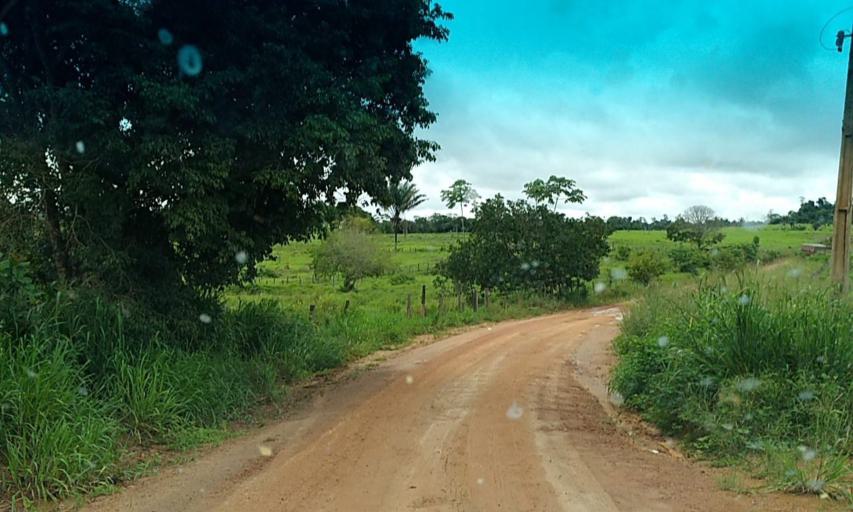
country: BR
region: Para
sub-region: Altamira
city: Altamira
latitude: -3.0780
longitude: -51.7048
